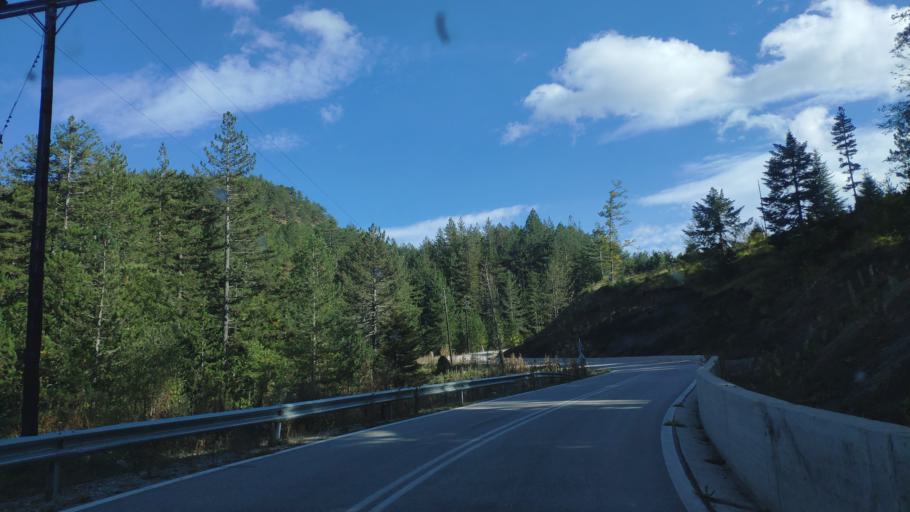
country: AL
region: Korce
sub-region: Rrethi i Devollit
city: Miras
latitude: 40.4097
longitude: 20.8765
